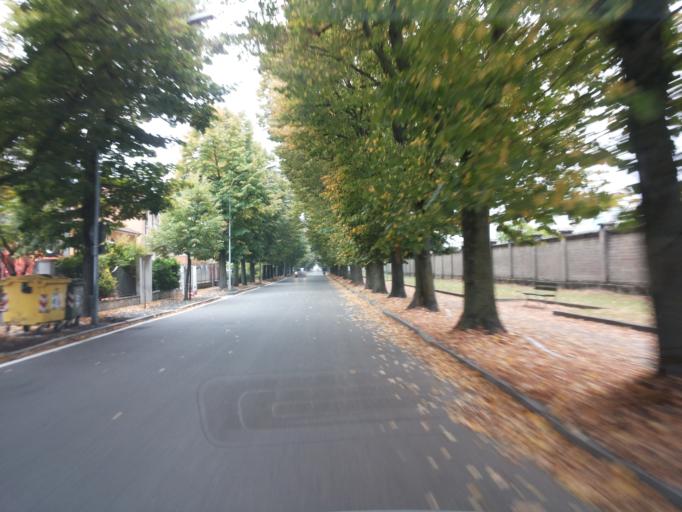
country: IT
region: Piedmont
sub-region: Provincia di Vercelli
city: Vercelli
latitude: 45.3323
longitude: 8.4349
